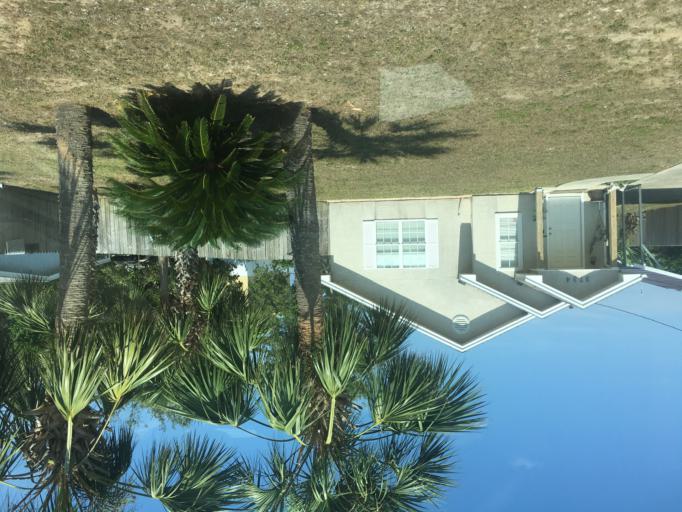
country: US
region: Florida
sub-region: Bay County
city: Lower Grand Lagoon
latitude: 30.1442
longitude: -85.7511
